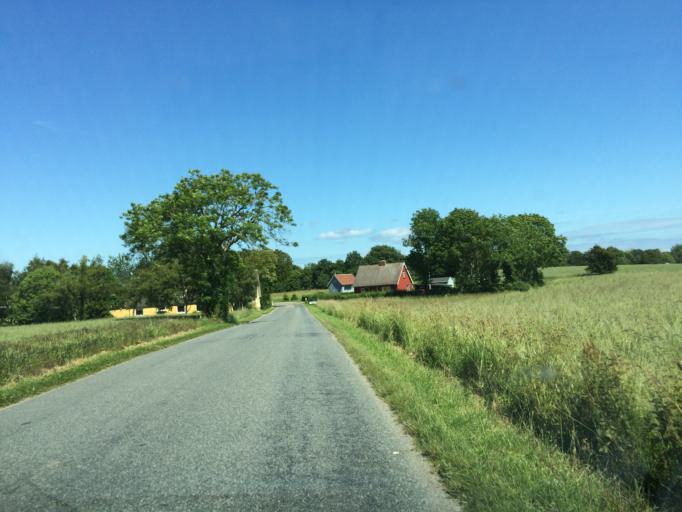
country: DK
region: Central Jutland
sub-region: Samso Kommune
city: Tranebjerg
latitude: 55.8302
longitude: 10.5788
